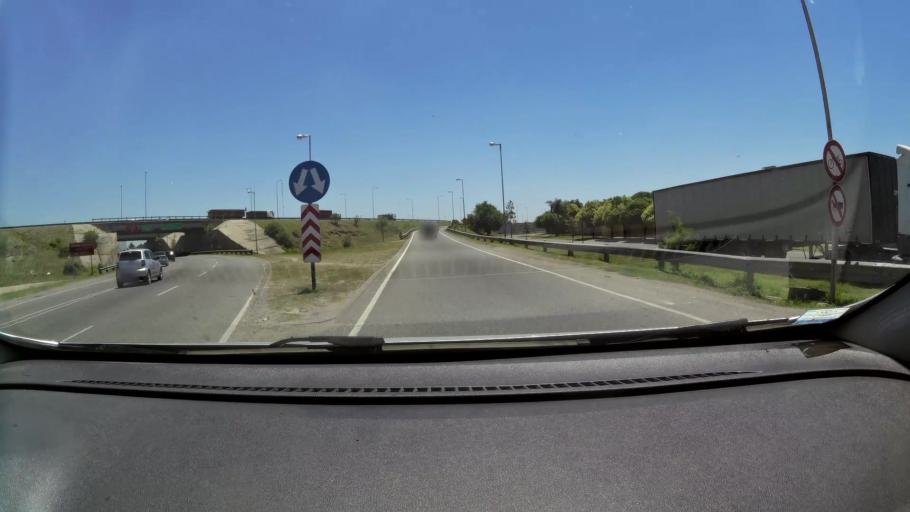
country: AR
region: Cordoba
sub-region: Departamento de Capital
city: Cordoba
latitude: -31.4430
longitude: -64.1223
